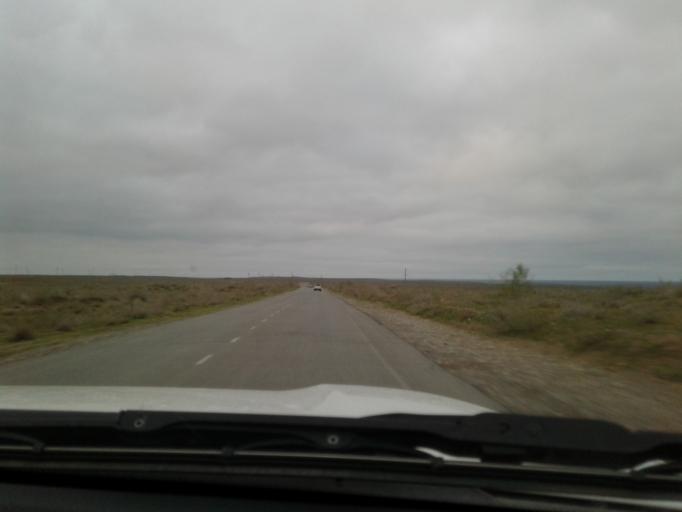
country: TM
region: Lebap
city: Farap
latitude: 39.0863
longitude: 63.7243
